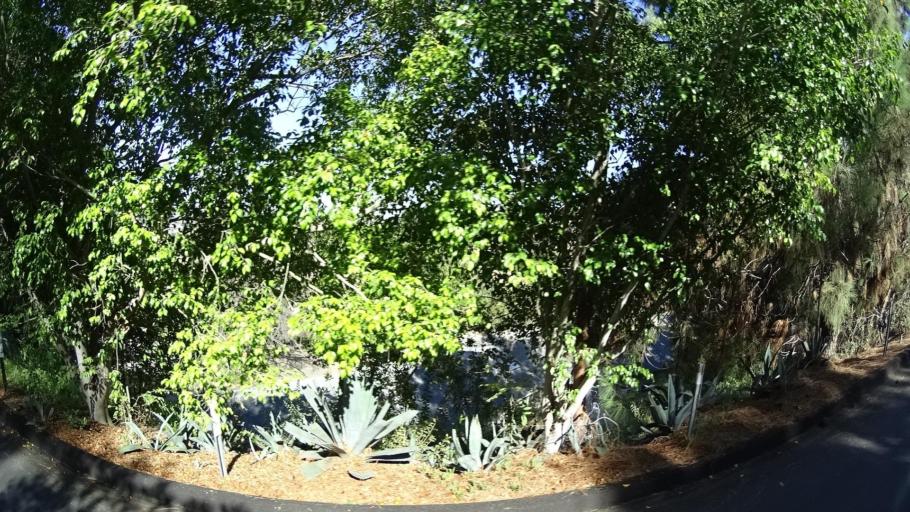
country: US
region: California
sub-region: San Diego County
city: Casa de Oro-Mount Helix
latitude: 32.7687
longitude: -116.9873
